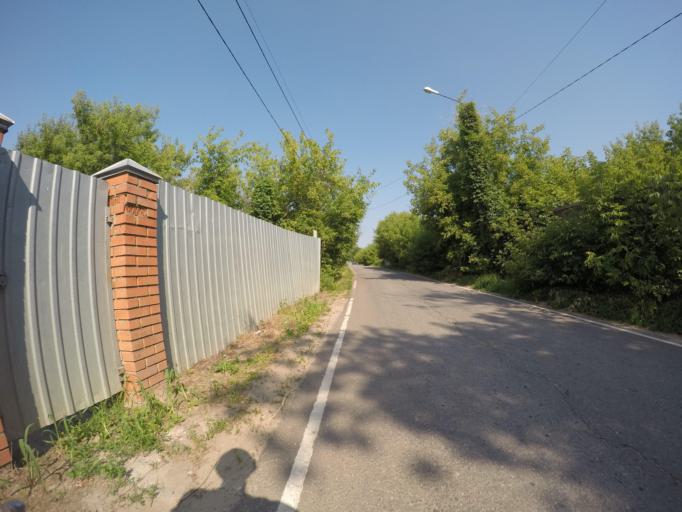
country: RU
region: Moskovskaya
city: Rechitsy
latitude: 55.6161
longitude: 38.5332
